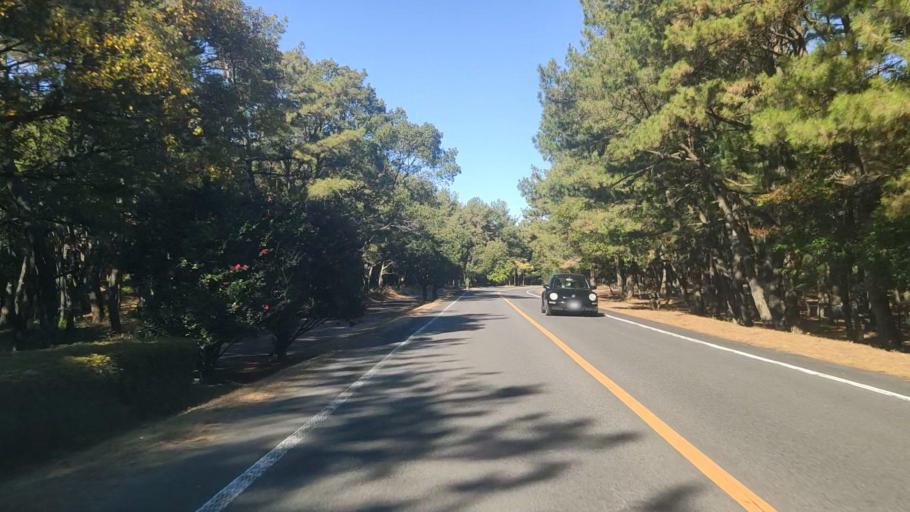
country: JP
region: Miyazaki
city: Miyazaki-shi
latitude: 31.9452
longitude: 131.4648
